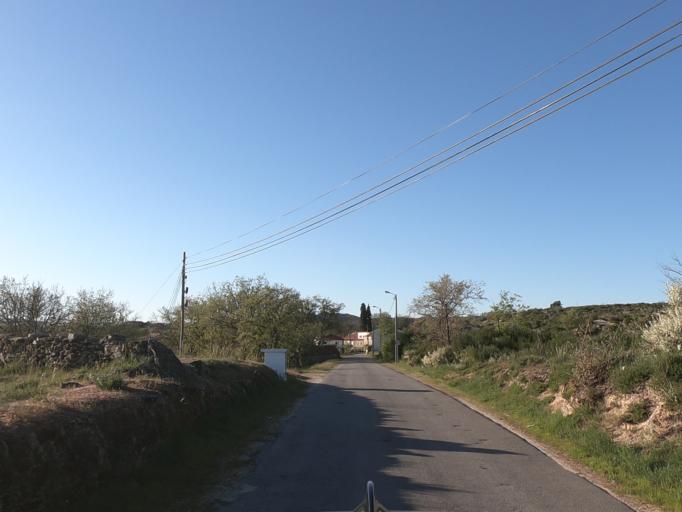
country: PT
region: Vila Real
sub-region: Vila Real
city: Vila Real
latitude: 41.3578
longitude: -7.6504
